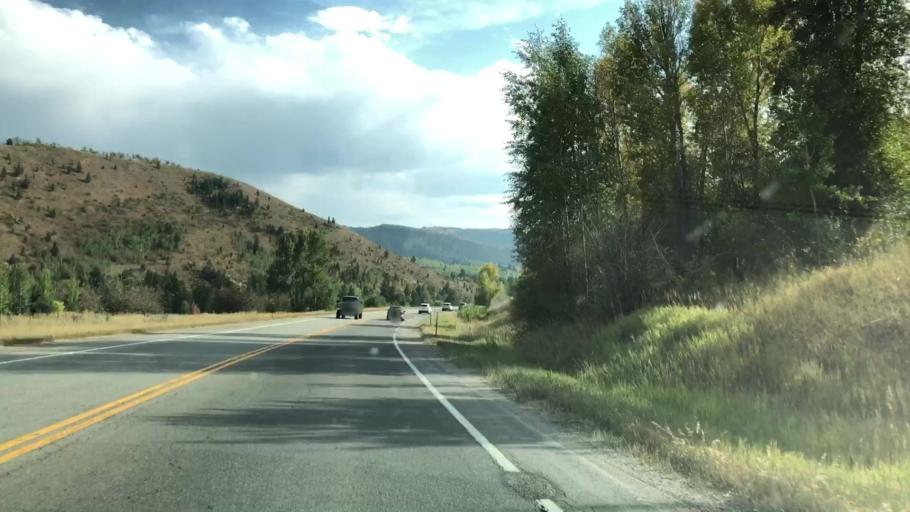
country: US
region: Wyoming
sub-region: Teton County
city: Hoback
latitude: 43.3530
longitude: -110.7201
